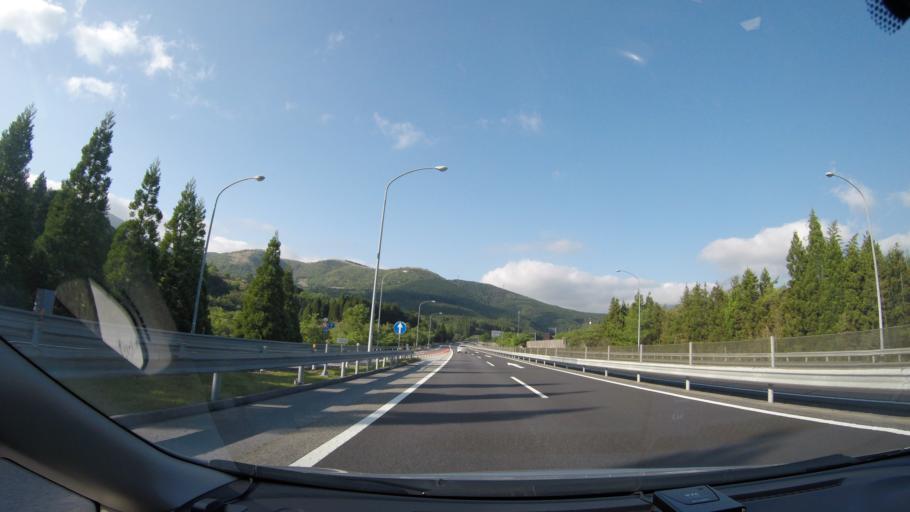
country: JP
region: Oita
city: Beppu
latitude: 33.2589
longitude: 131.3304
